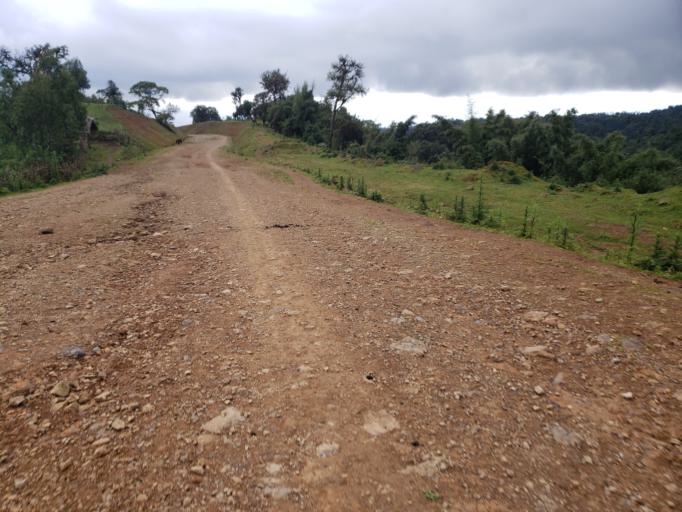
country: ET
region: Oromiya
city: Dodola
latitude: 6.6872
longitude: 39.3697
